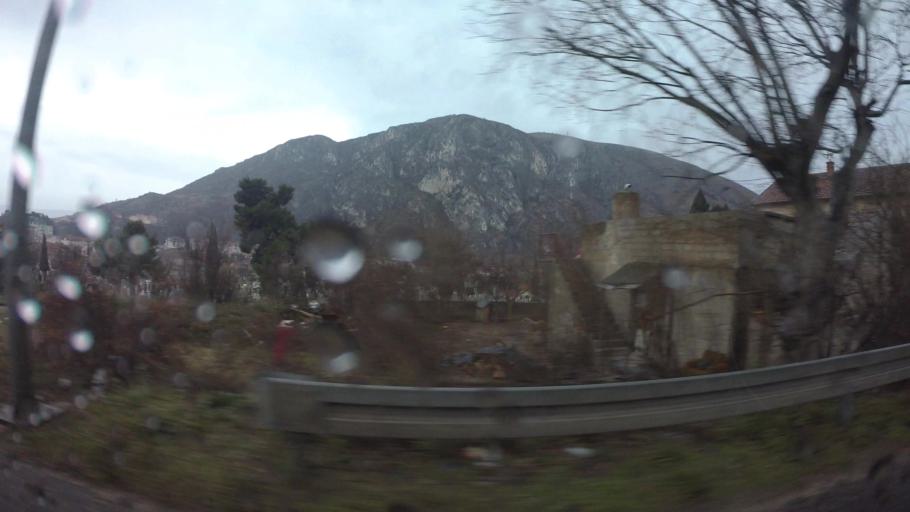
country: BA
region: Federation of Bosnia and Herzegovina
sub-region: Hercegovacko-Bosanski Kanton
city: Mostar
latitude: 43.3309
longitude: 17.8211
